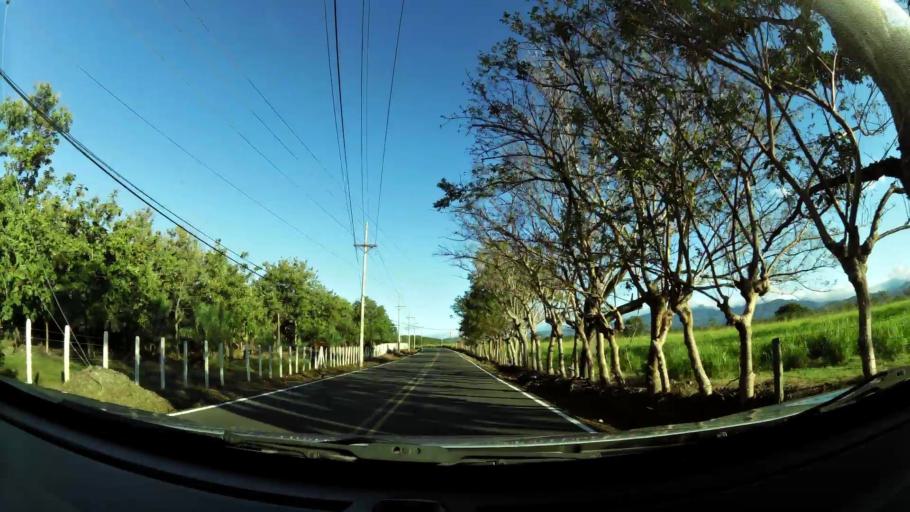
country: CR
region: Puntarenas
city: Miramar
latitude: 10.0971
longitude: -84.8208
